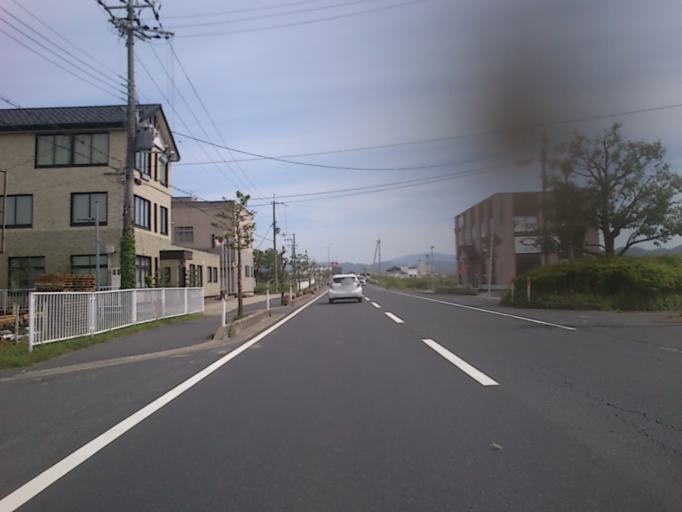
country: JP
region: Kyoto
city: Miyazu
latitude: 35.6166
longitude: 135.0769
